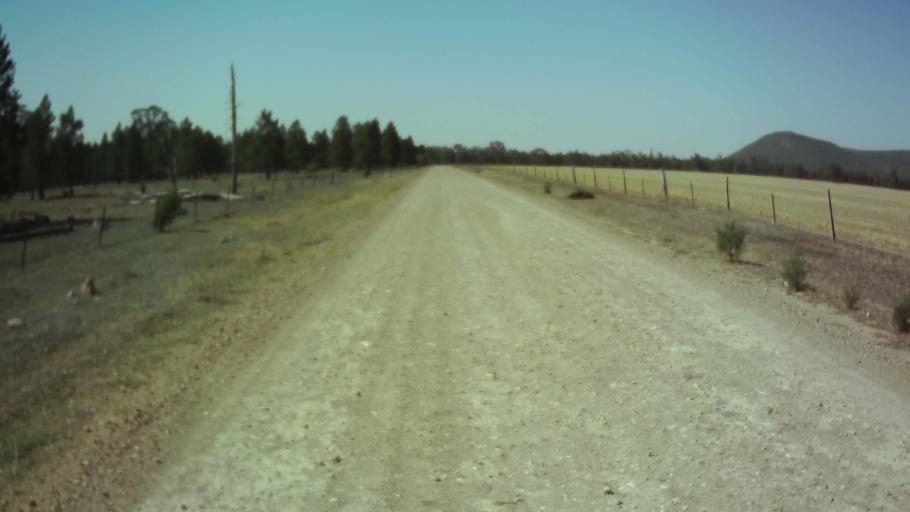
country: AU
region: New South Wales
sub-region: Weddin
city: Grenfell
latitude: -33.9252
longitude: 147.9319
